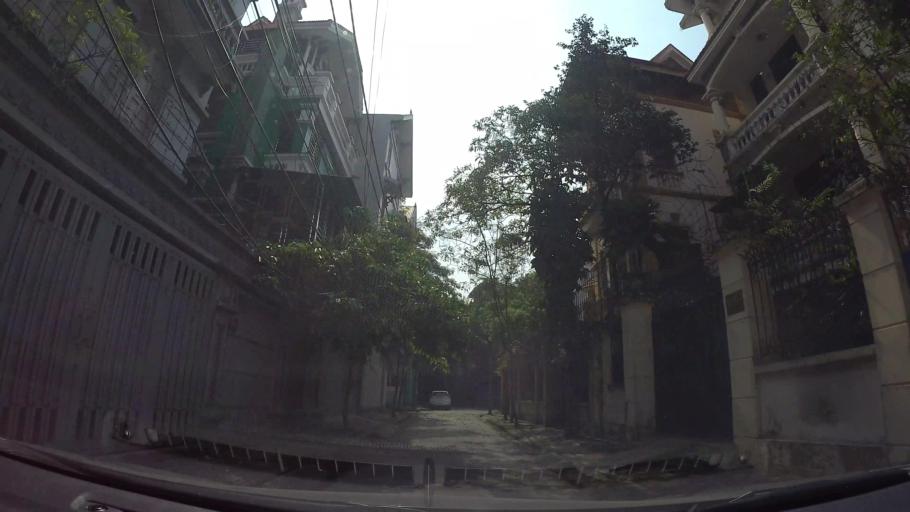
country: VN
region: Ha Noi
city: Van Dien
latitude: 20.9762
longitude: 105.8339
